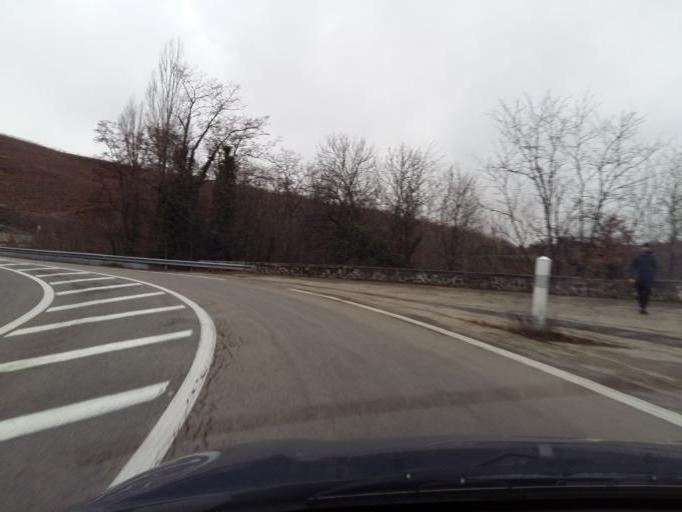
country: FR
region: Rhone-Alpes
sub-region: Departement de l'Ardeche
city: Andance
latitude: 45.2508
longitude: 4.7710
